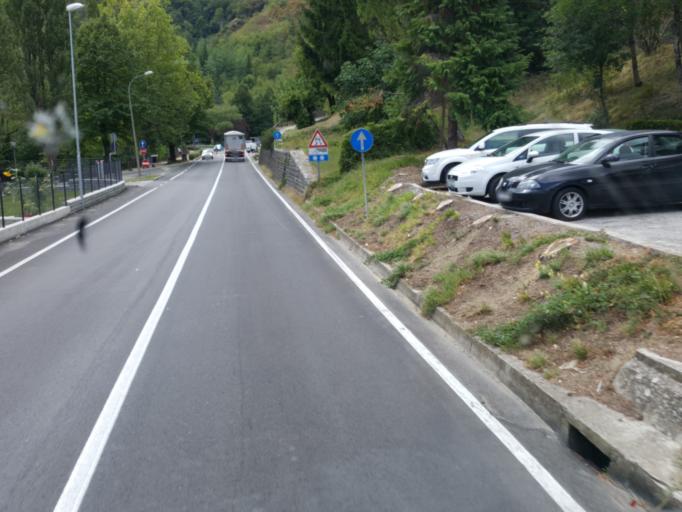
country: IT
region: Emilia-Romagna
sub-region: Forli-Cesena
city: San Piero in Bagno
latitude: 43.8328
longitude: 11.9570
